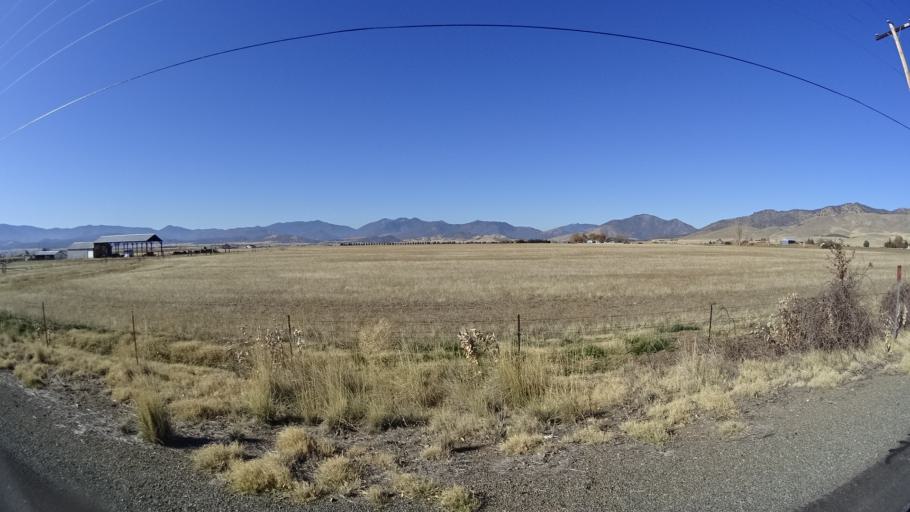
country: US
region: California
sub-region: Siskiyou County
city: Montague
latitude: 41.7588
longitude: -122.5247
